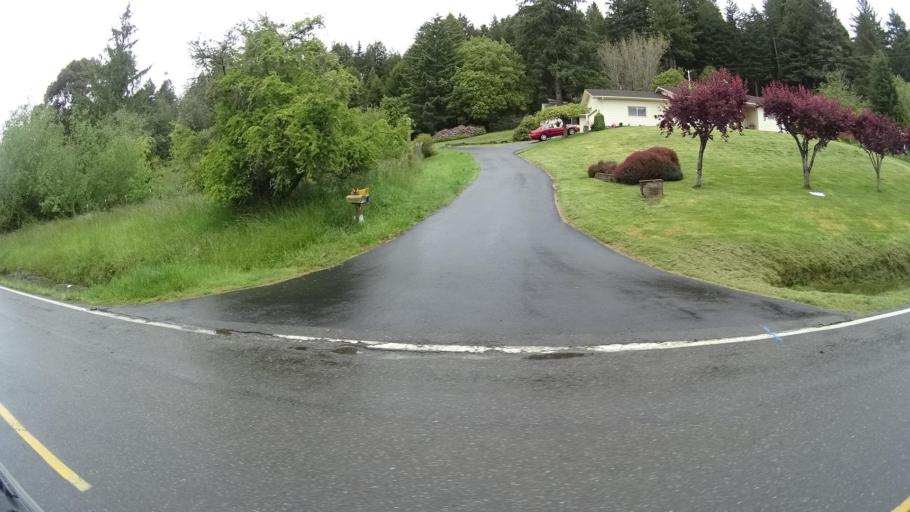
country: US
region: California
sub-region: Humboldt County
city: Bayside
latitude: 40.8393
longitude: -124.0572
